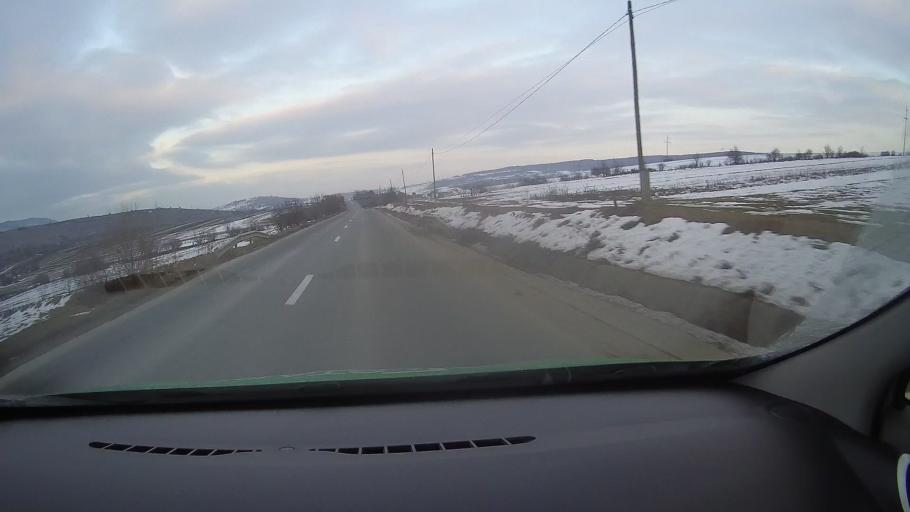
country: RO
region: Harghita
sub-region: Comuna Lupeni
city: Lupeni
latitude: 46.3568
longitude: 25.2064
